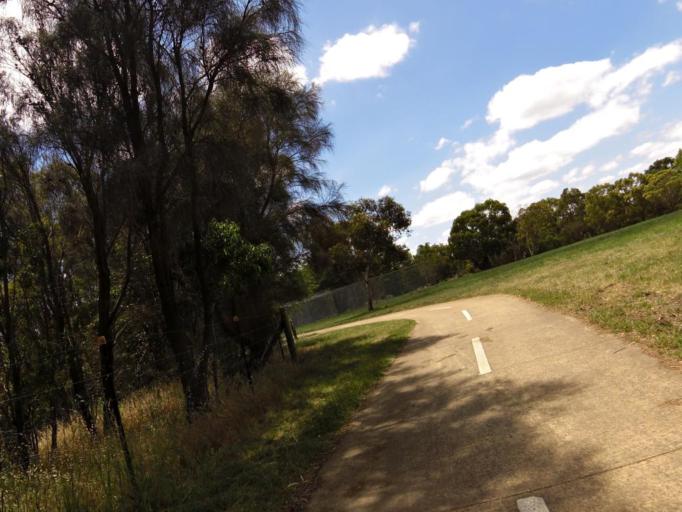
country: AU
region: Victoria
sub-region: Moreland
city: Fawkner
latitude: -37.6952
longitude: 144.9768
